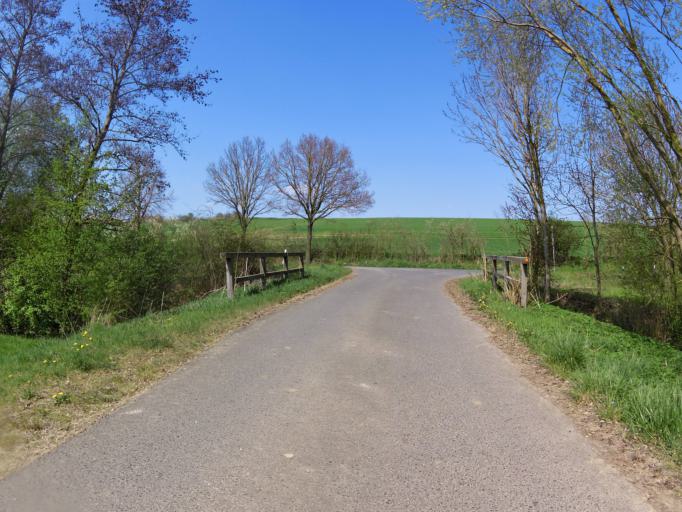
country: DE
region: Bavaria
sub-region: Regierungsbezirk Unterfranken
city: Dettelbach
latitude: 49.8214
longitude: 10.1368
